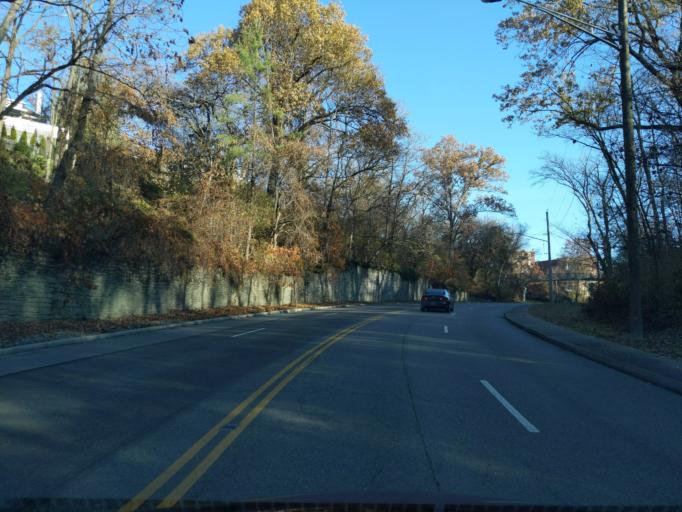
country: US
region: Kentucky
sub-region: Campbell County
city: Dayton
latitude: 39.1299
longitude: -84.4645
